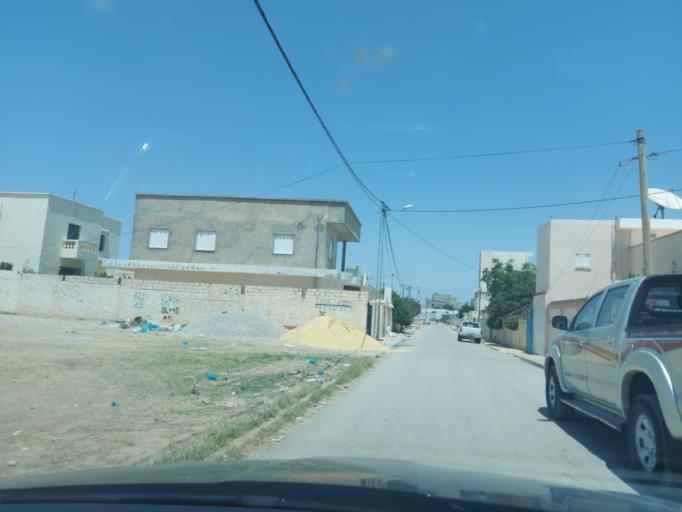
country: TN
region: Silyanah
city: Siliana
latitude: 36.0863
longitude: 9.3652
